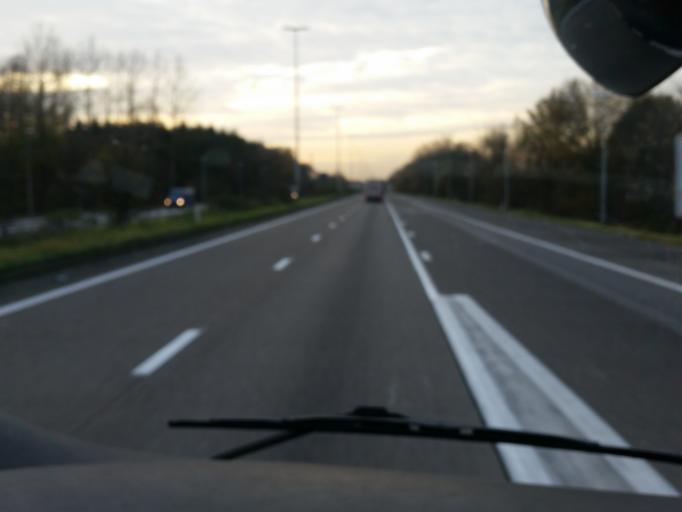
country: BE
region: Flanders
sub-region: Provincie Antwerpen
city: Turnhout
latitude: 51.2982
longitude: 4.9460
